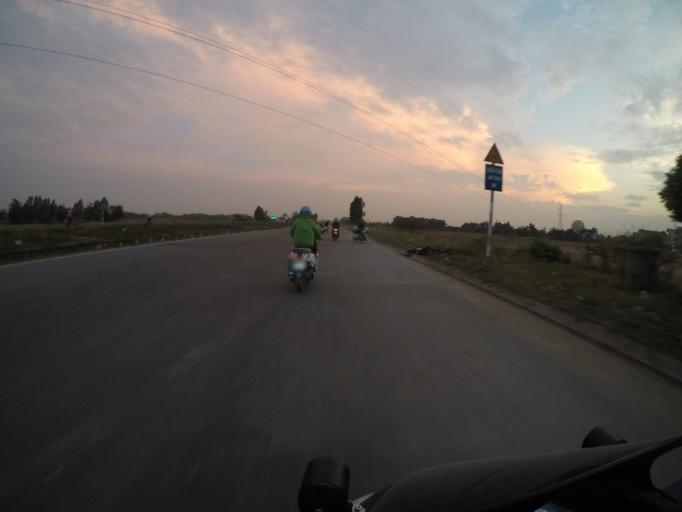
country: VN
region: Vinh Phuc
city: Phuc Yen
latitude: 21.2654
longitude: 105.7228
